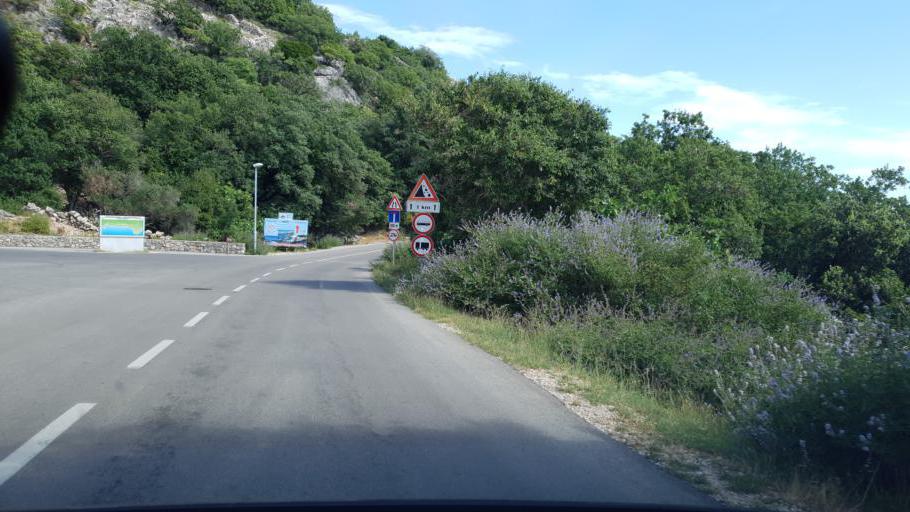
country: HR
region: Primorsko-Goranska
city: Punat
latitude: 44.9655
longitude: 14.6794
